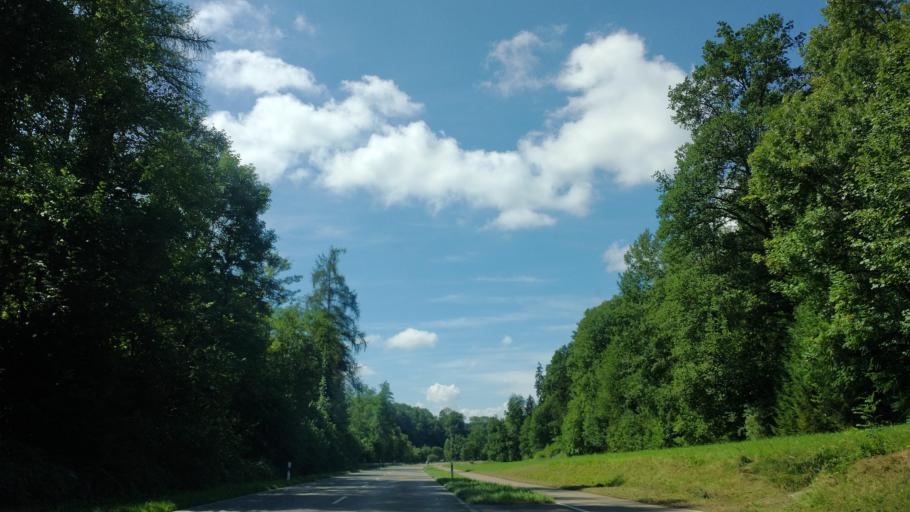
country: DE
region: Baden-Wuerttemberg
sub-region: Tuebingen Region
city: Tettnang
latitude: 47.6442
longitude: 9.6431
